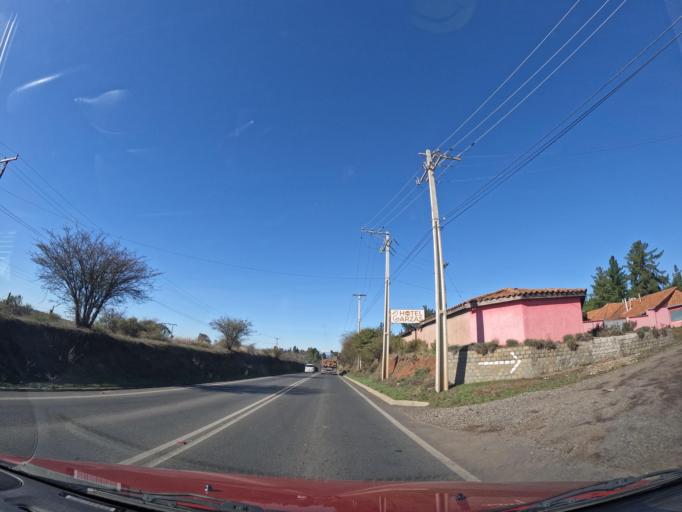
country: CL
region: Maule
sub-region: Provincia de Cauquenes
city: Cauquenes
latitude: -35.9599
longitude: -72.2622
